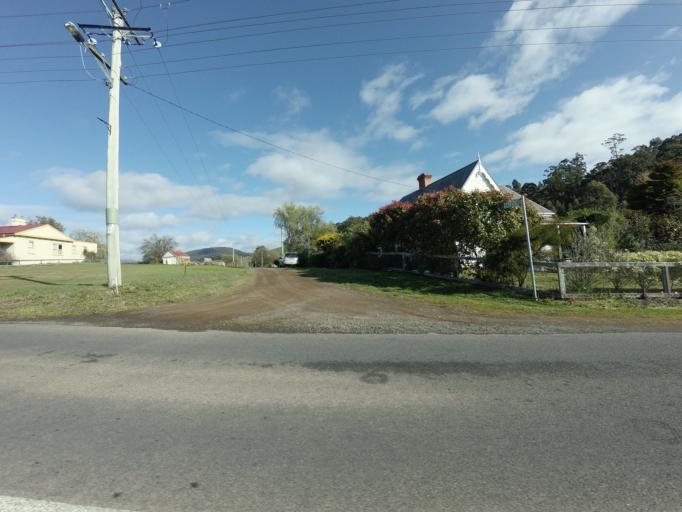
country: AU
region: Tasmania
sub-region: Huon Valley
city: Cygnet
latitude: -43.3163
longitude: 147.0114
